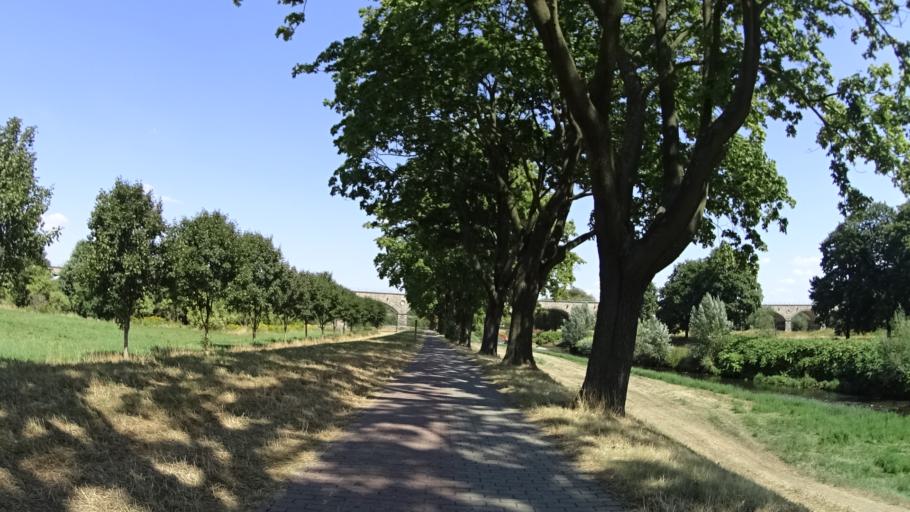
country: DE
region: Saxony
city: Zittau
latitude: 50.8913
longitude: 14.8270
